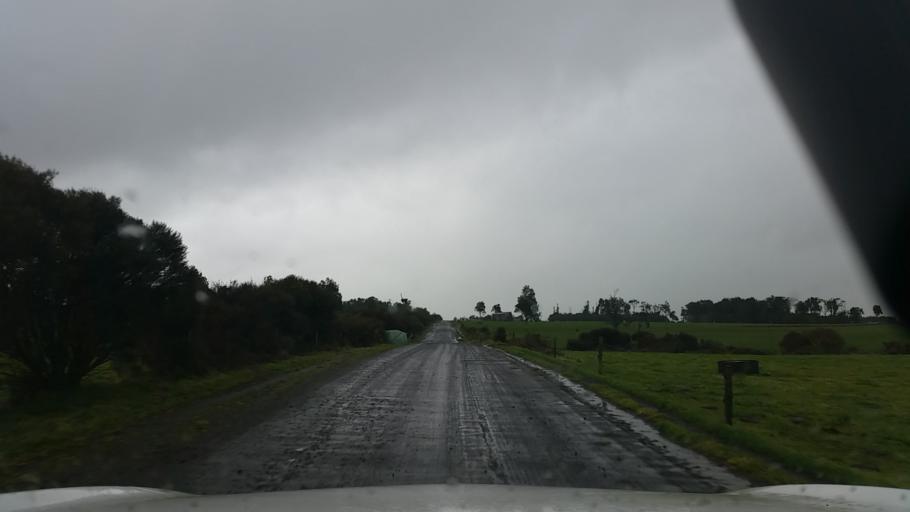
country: NZ
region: Taranaki
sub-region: South Taranaki District
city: Eltham
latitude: -39.2793
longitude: 174.1780
